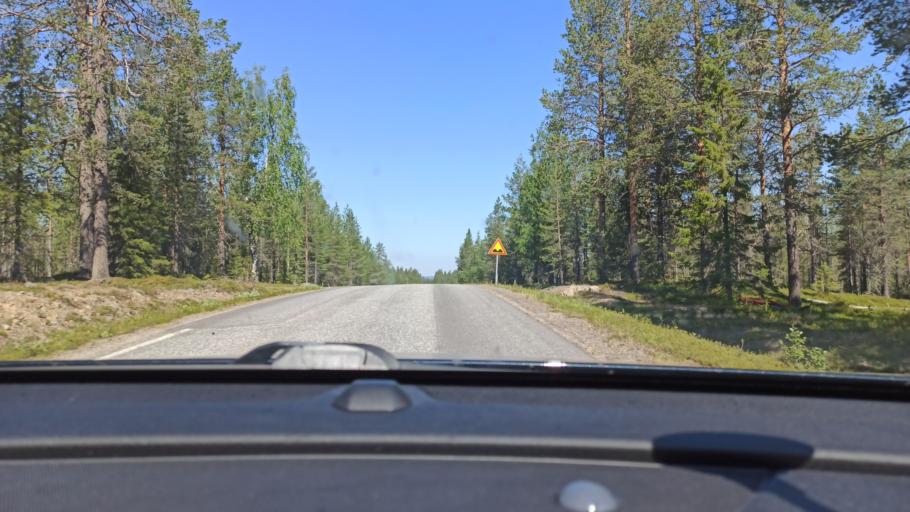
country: FI
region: Lapland
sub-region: Tunturi-Lappi
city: Kolari
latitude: 67.6752
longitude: 24.1447
